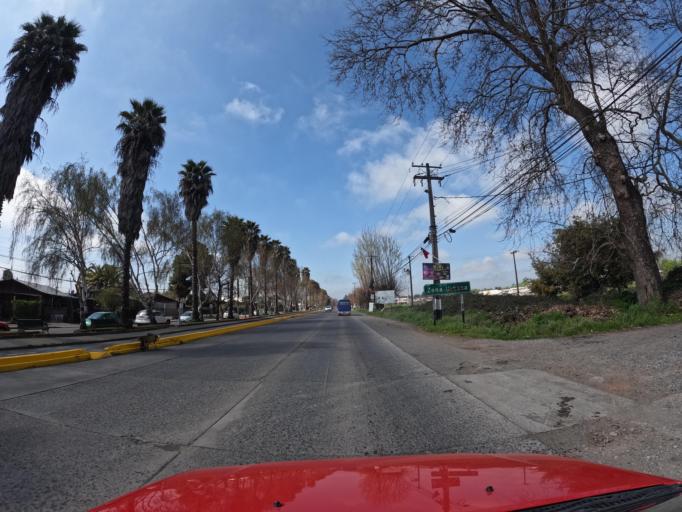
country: CL
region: Maule
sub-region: Provincia de Curico
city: Molina
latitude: -35.0512
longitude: -71.2797
